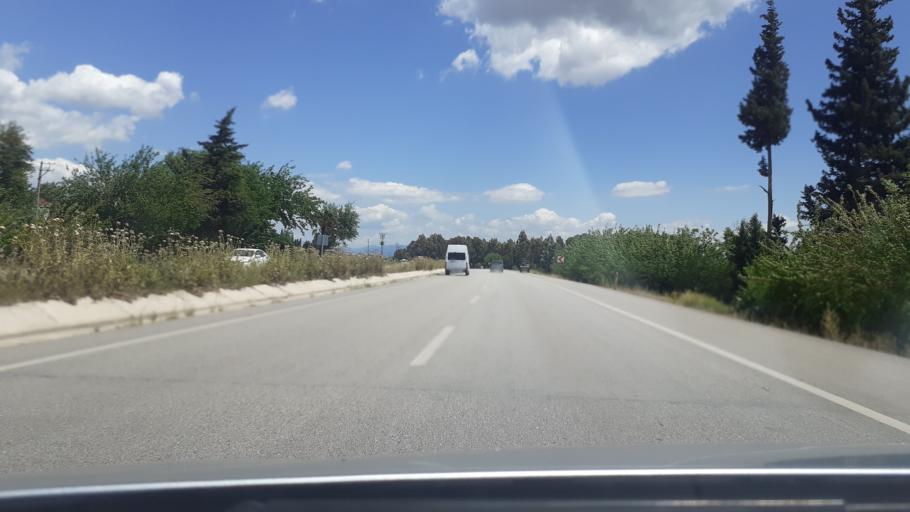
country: TR
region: Hatay
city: Kirikhan
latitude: 36.4608
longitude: 36.3300
